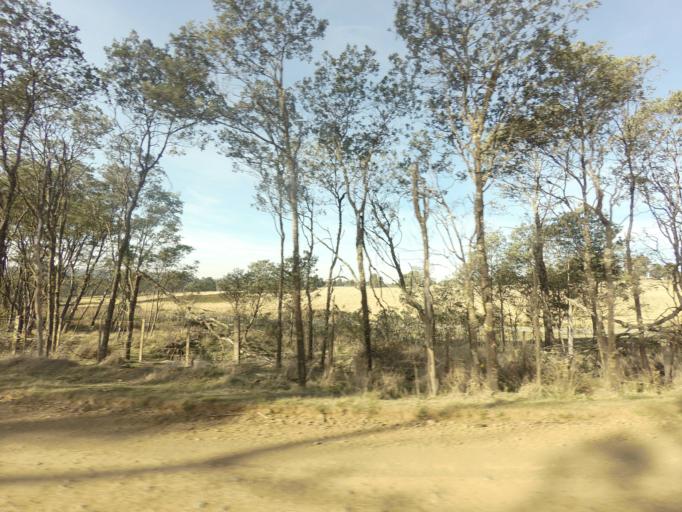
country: AU
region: Tasmania
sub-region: Brighton
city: Bridgewater
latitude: -42.4847
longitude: 147.3867
